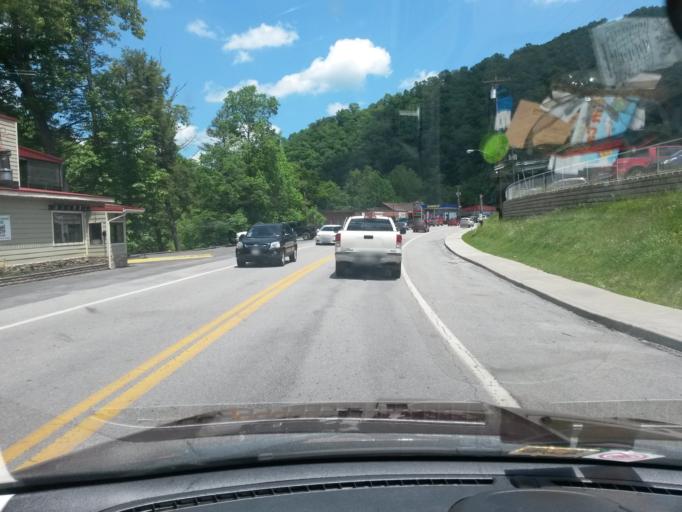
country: US
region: West Virginia
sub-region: Wyoming County
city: Pineville
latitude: 37.5792
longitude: -81.5368
